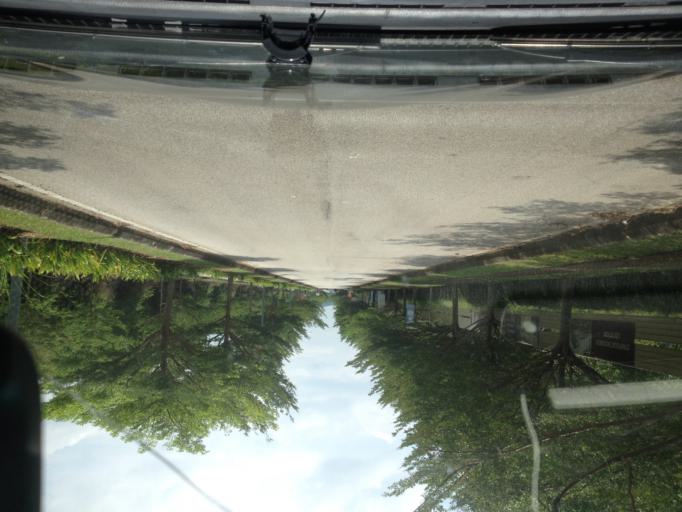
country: MY
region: Kedah
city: Sungai Petani
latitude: 5.6148
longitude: 100.5491
